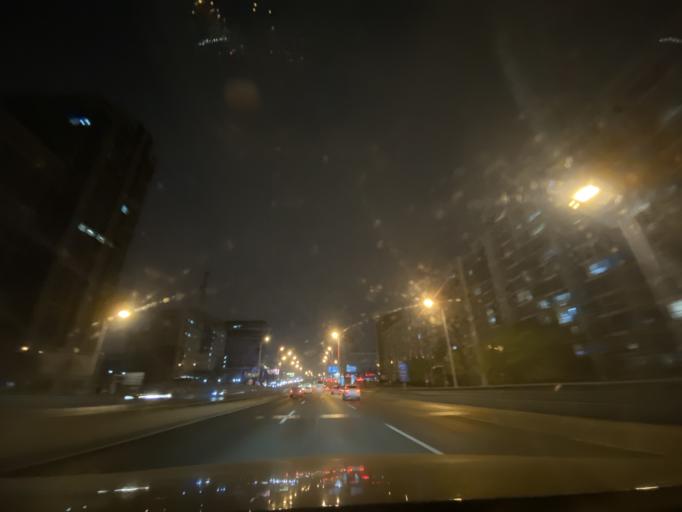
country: CN
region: Beijing
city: Baizhifang
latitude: 39.8959
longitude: 116.3225
